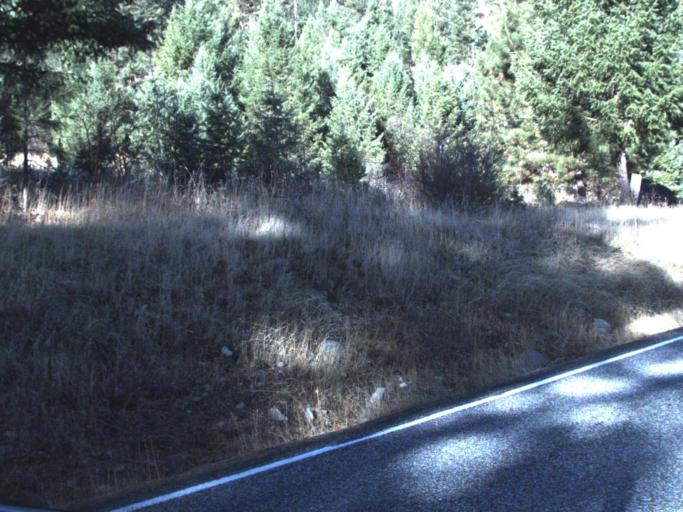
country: US
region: Washington
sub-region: Ferry County
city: Republic
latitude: 48.5659
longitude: -118.7476
